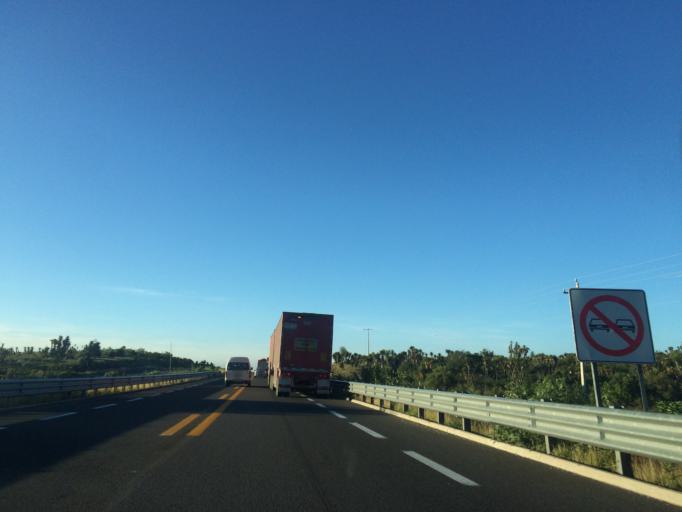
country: MX
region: Puebla
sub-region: Tehuacan
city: Magdalena Cuayucatepec
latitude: 18.5857
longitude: -97.4681
